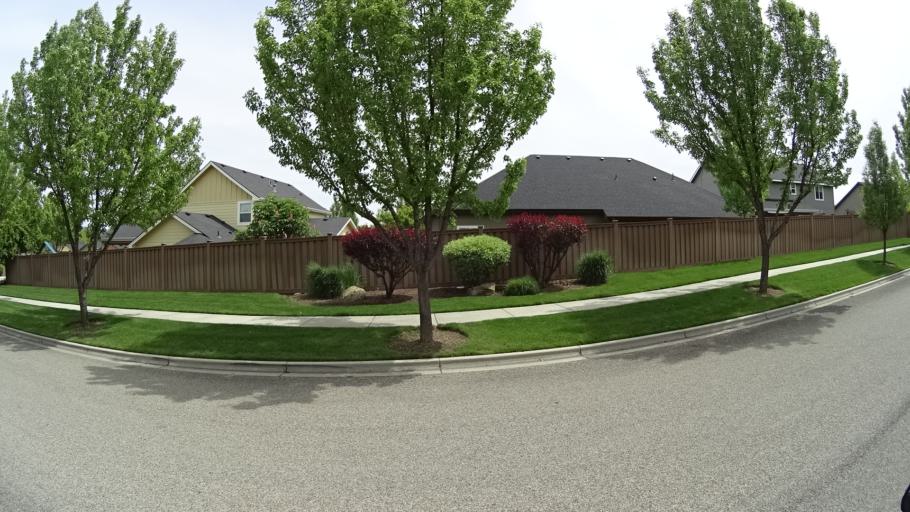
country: US
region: Idaho
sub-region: Ada County
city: Meridian
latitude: 43.5594
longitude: -116.3245
